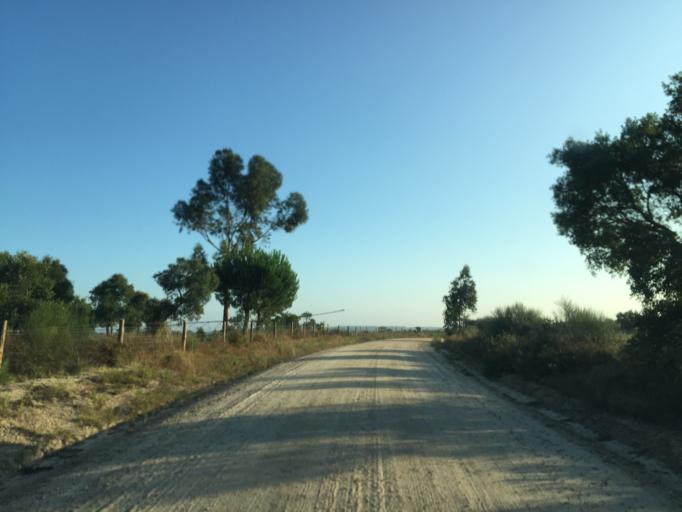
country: PT
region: Portalegre
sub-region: Ponte de Sor
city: Santo Andre
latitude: 39.1093
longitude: -8.3437
